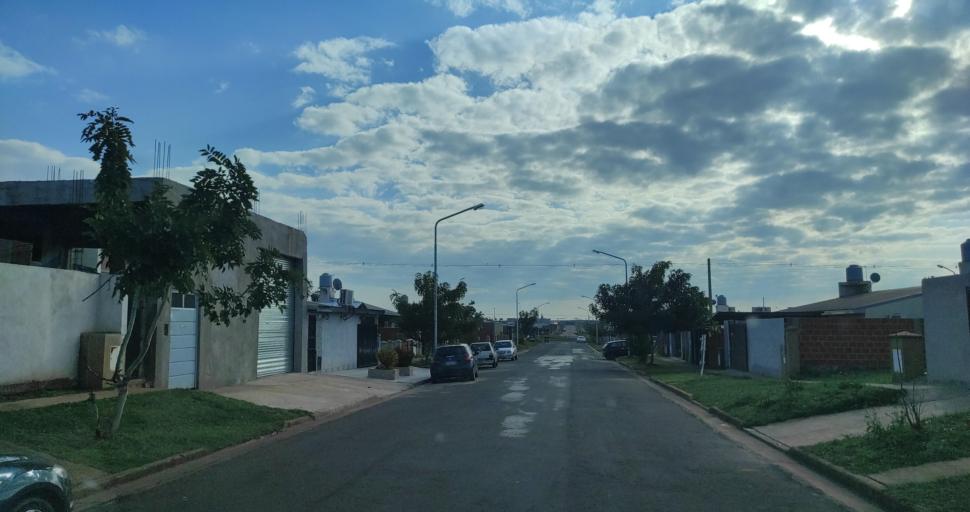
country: AR
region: Misiones
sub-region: Departamento de Capital
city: Posadas
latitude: -27.4085
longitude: -55.9859
